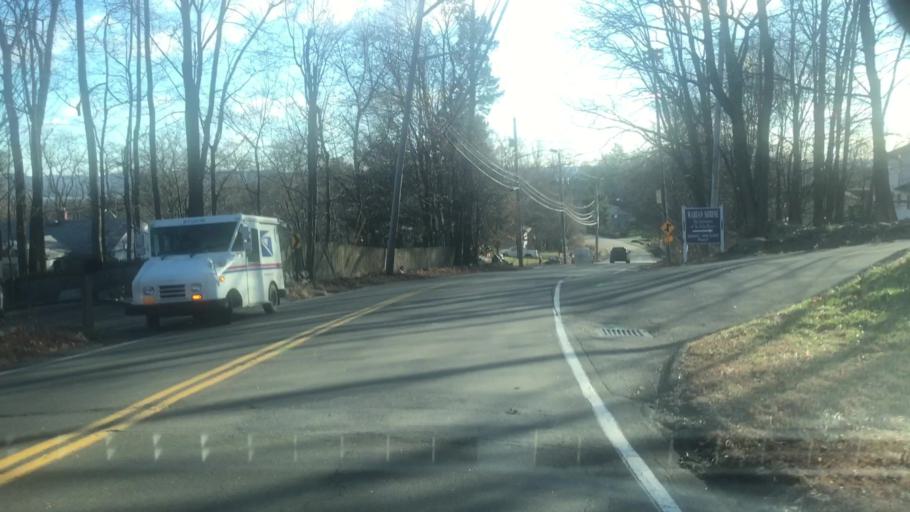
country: US
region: New York
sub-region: Rockland County
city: Thiells
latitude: 41.2214
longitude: -74.0059
